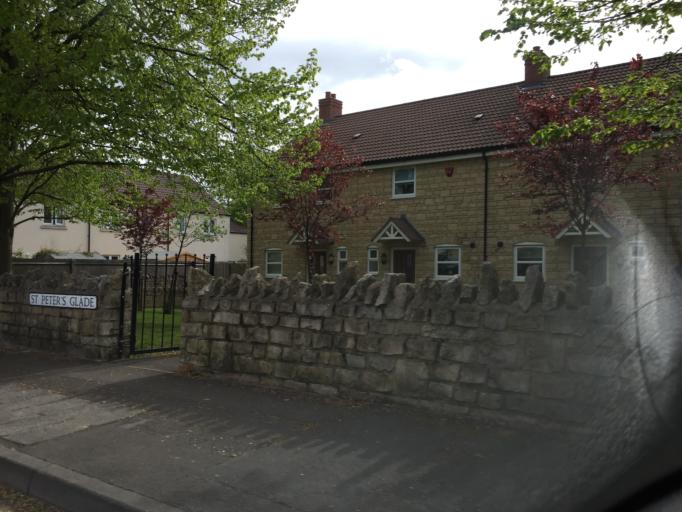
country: GB
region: England
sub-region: Bath and North East Somerset
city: Radstock
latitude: 51.2835
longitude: -2.4690
